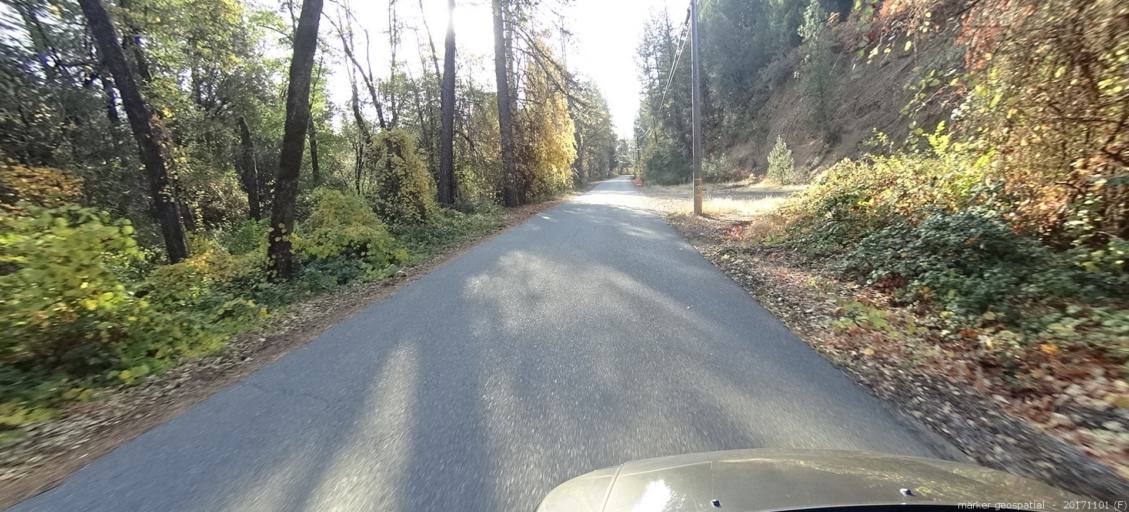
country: US
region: California
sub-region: Shasta County
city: Shasta Lake
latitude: 40.8139
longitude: -122.3270
